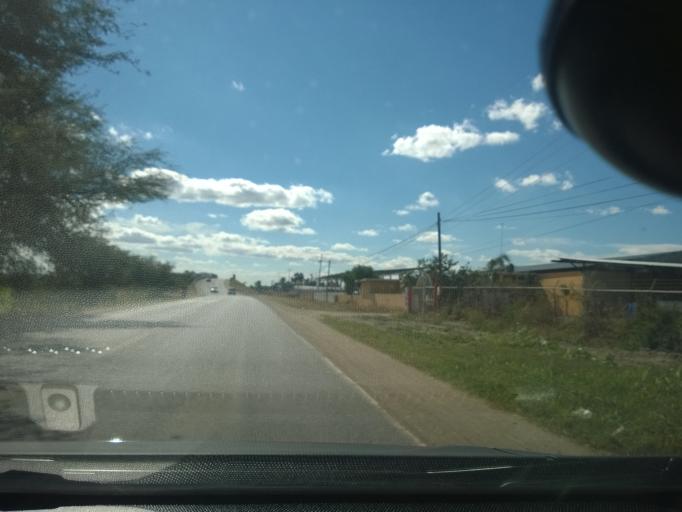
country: MX
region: Guanajuato
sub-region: Silao de la Victoria
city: La Aldea
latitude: 20.8981
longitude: -101.4844
